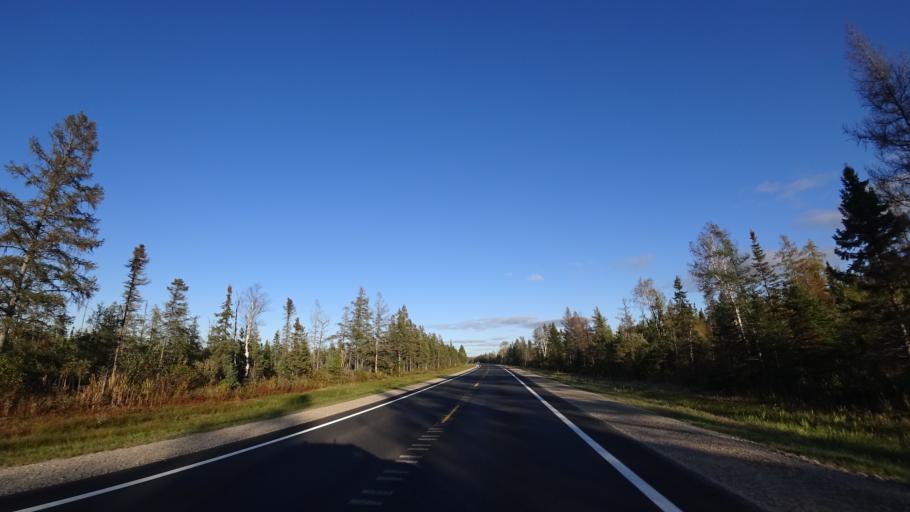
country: US
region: Michigan
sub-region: Luce County
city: Newberry
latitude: 46.3354
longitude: -85.8526
